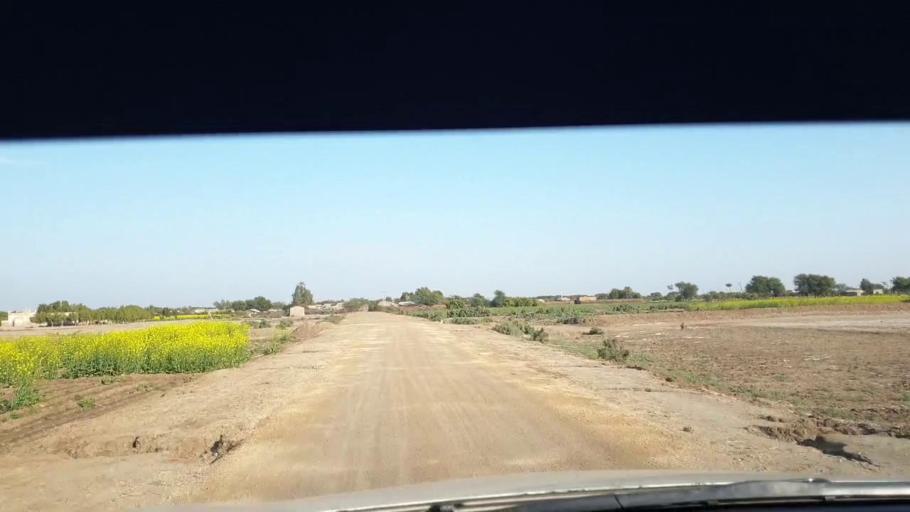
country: PK
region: Sindh
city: Berani
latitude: 25.7899
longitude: 68.9309
